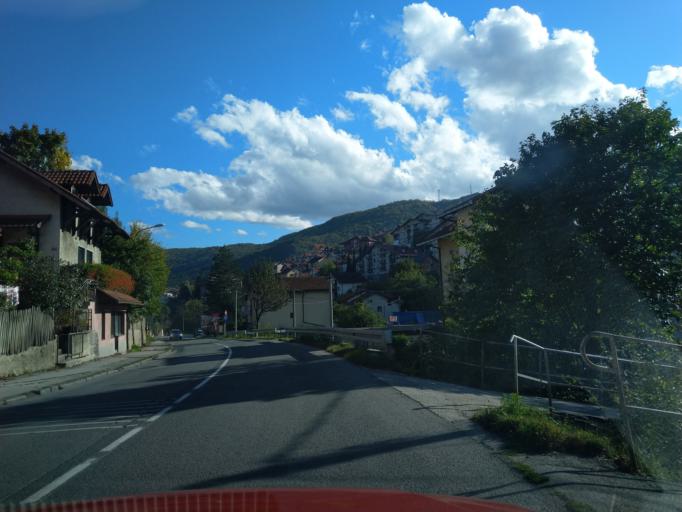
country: RS
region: Central Serbia
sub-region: Zlatiborski Okrug
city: Uzice
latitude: 43.8606
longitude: 19.8268
